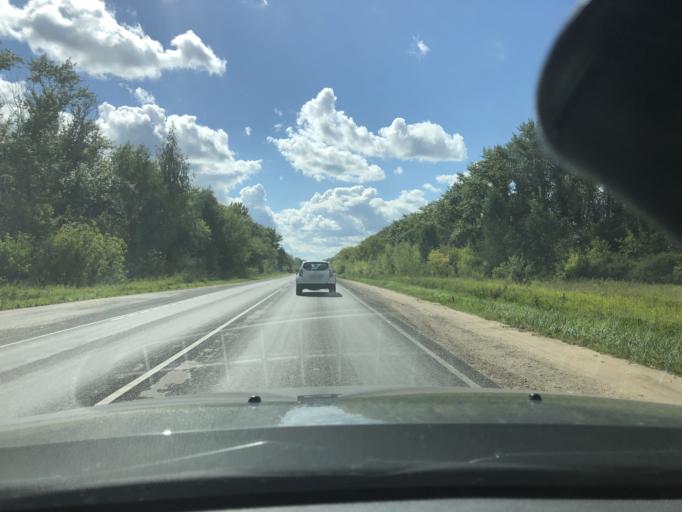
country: RU
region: Tula
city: Kimovsk
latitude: 53.9721
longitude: 38.5011
